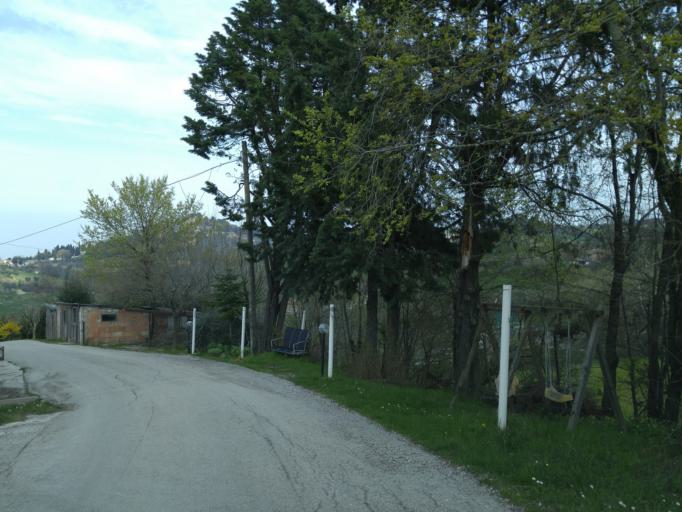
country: IT
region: The Marches
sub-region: Provincia di Pesaro e Urbino
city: Villanova
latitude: 43.7279
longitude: 12.9340
